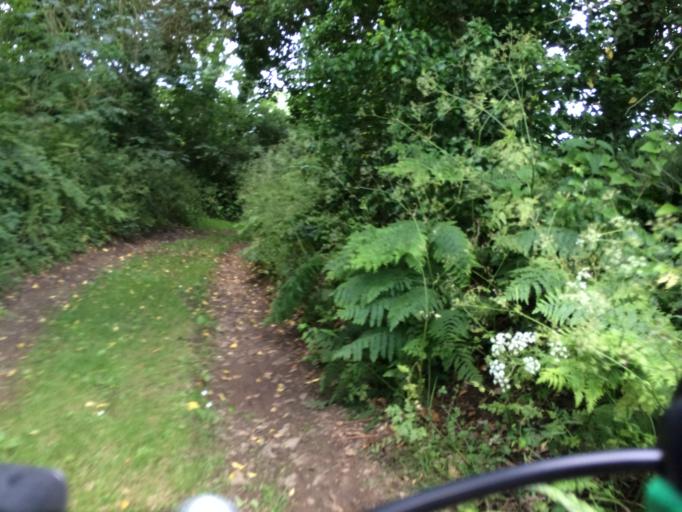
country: FR
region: Brittany
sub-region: Departement du Finistere
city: Logonna-Daoulas
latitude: 48.3248
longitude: -4.2940
